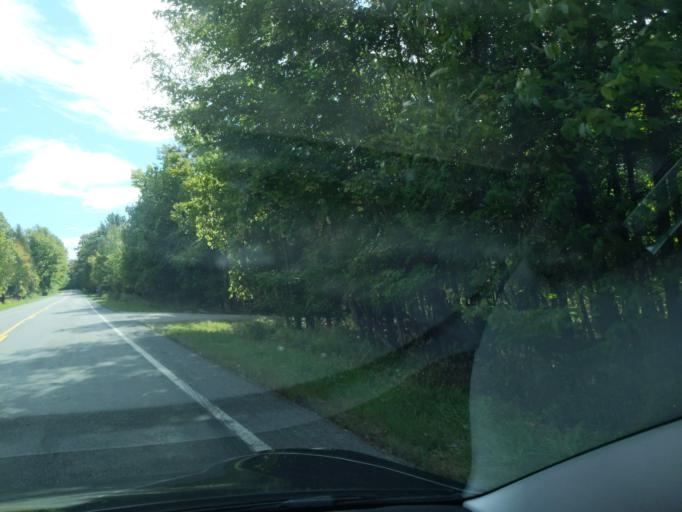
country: US
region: Michigan
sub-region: Antrim County
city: Bellaire
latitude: 45.0309
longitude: -85.2957
